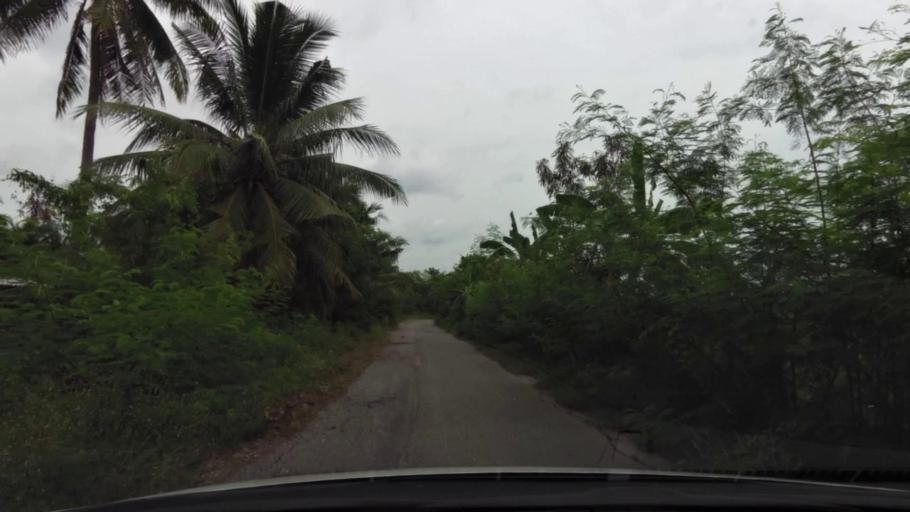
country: TH
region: Samut Sakhon
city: Ban Phaeo
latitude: 13.6017
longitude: 100.0335
